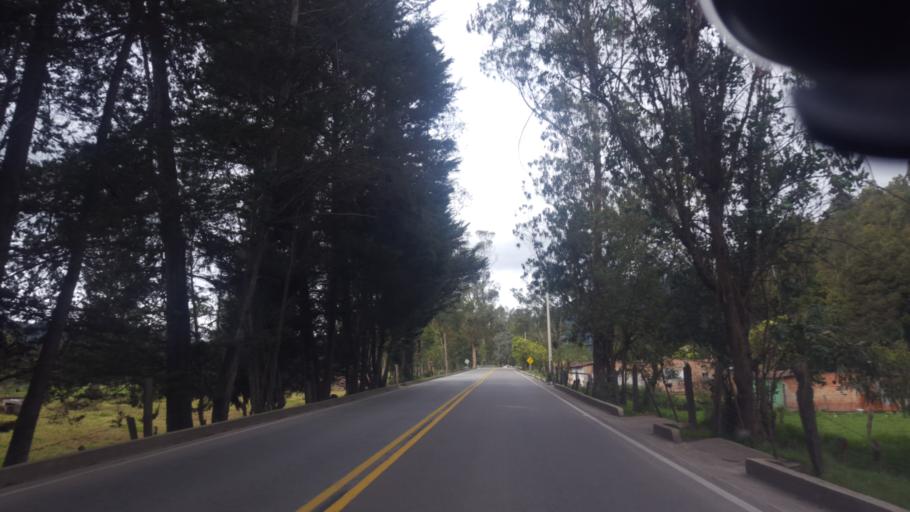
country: CO
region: Boyaca
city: Belen
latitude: 5.9740
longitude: -72.9279
